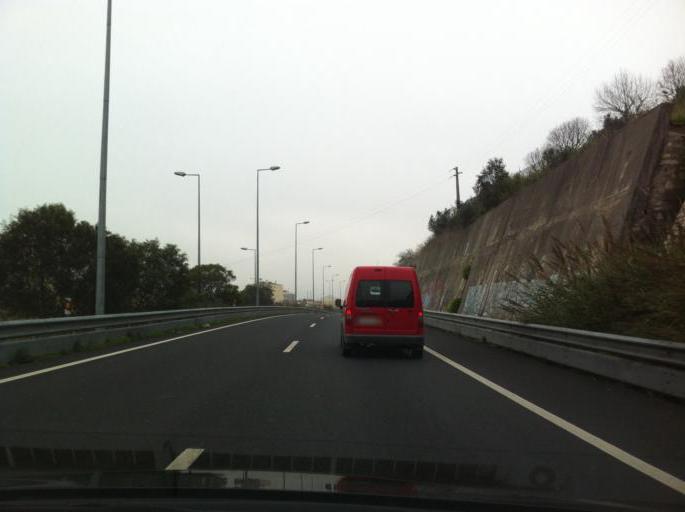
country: PT
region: Lisbon
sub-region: Odivelas
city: Pontinha
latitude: 38.7691
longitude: -9.2109
